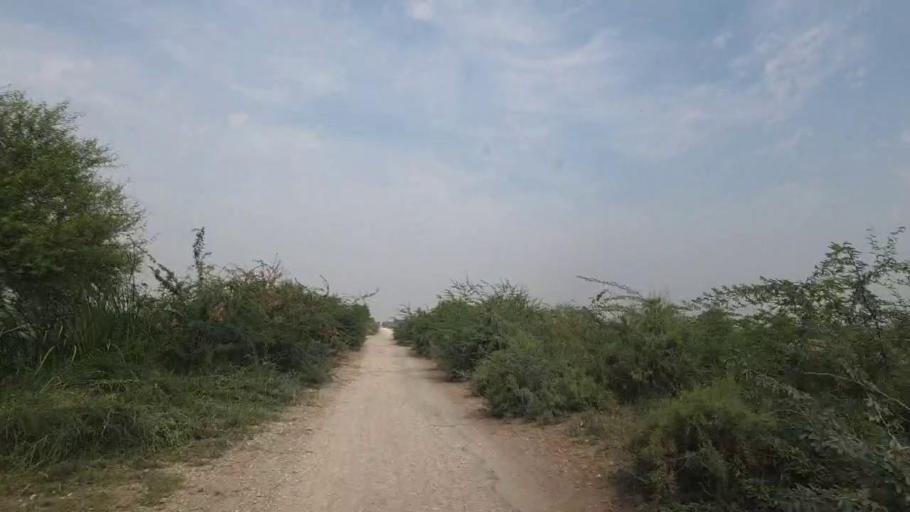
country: PK
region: Sindh
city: Rajo Khanani
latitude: 24.9776
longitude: 68.9951
